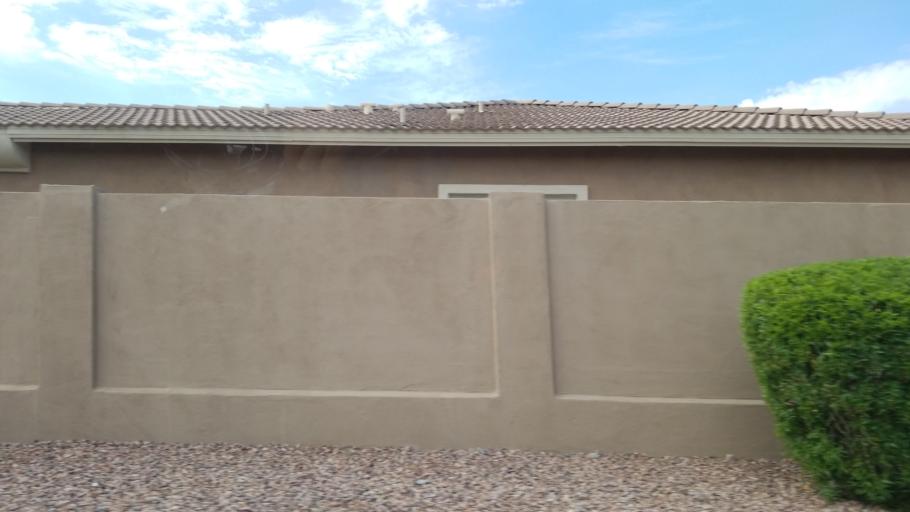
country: US
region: Arizona
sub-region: Maricopa County
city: Paradise Valley
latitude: 33.6149
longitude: -112.0571
